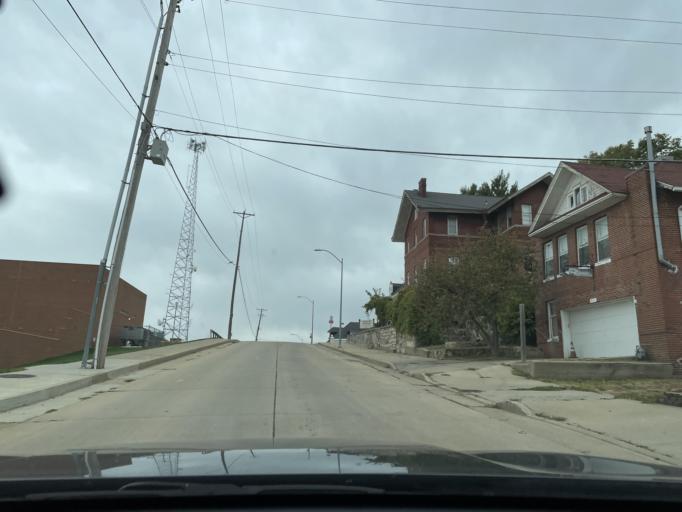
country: US
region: Missouri
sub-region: Buchanan County
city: Saint Joseph
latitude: 39.7698
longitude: -94.8534
